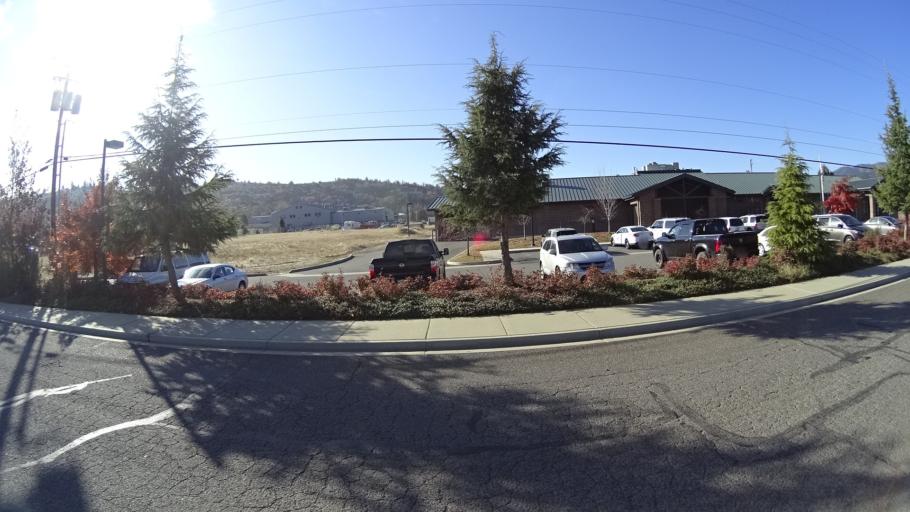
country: US
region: California
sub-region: Siskiyou County
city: Yreka
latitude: 41.7087
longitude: -122.6345
